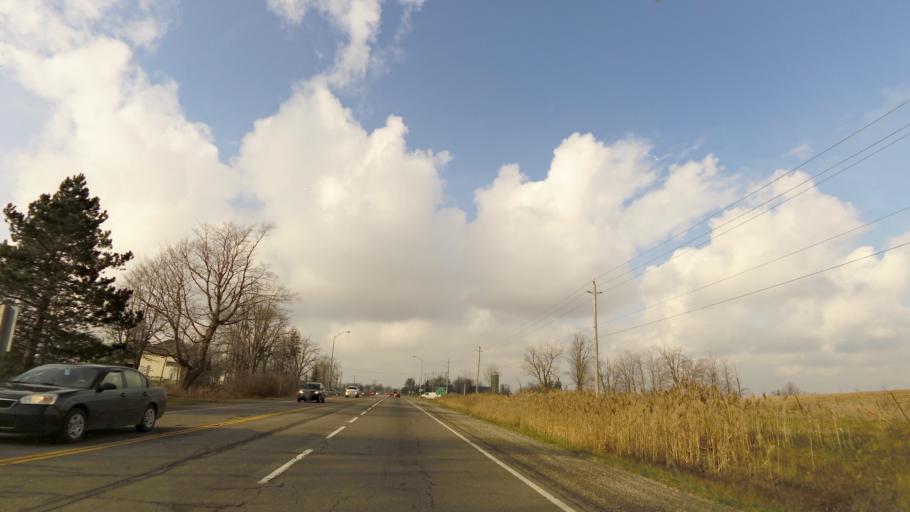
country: CA
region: Ontario
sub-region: Wellington County
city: Guelph
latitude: 43.4338
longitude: -80.0987
